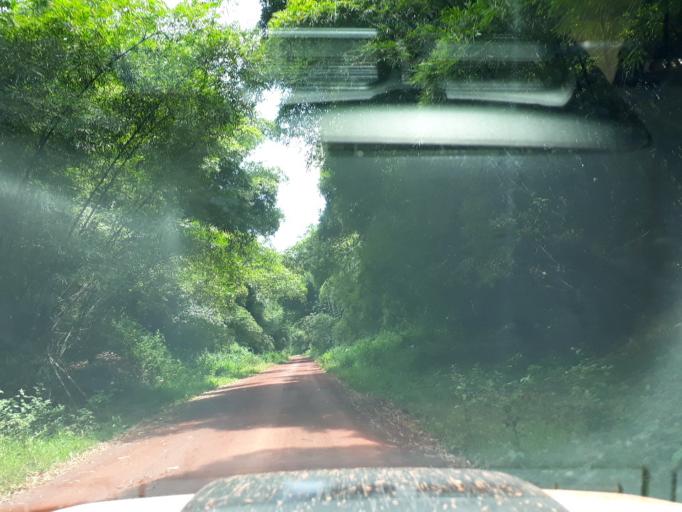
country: CD
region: Eastern Province
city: Buta
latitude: 2.5707
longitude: 24.8239
